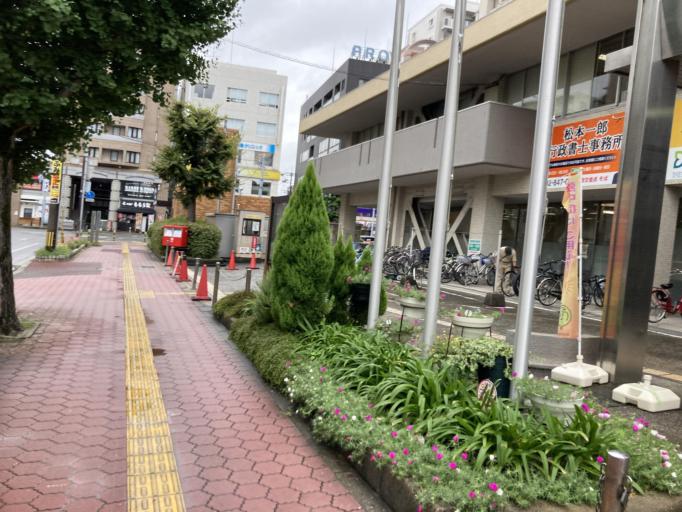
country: JP
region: Fukuoka
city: Fukuoka-shi
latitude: 33.5818
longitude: 130.3488
